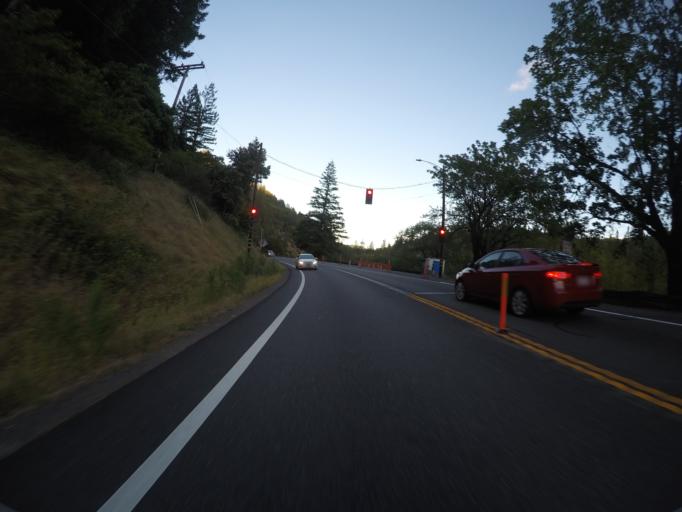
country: US
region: California
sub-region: Humboldt County
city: Redway
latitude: 39.8921
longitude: -123.7533
